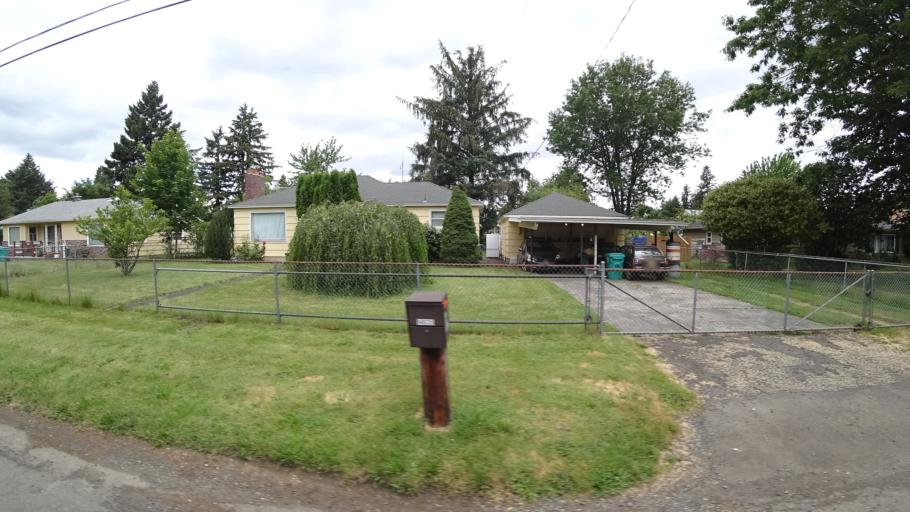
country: US
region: Oregon
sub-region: Clackamas County
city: Happy Valley
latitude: 45.4962
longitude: -122.5121
